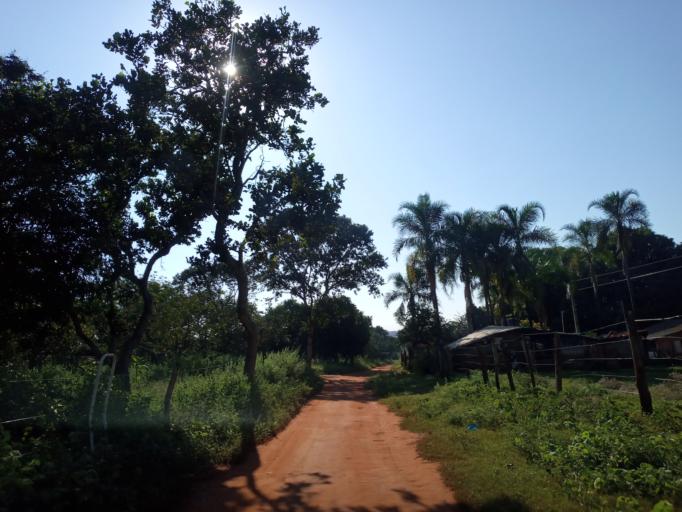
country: BR
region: Minas Gerais
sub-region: Ituiutaba
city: Ituiutaba
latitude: -18.9754
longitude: -49.5002
